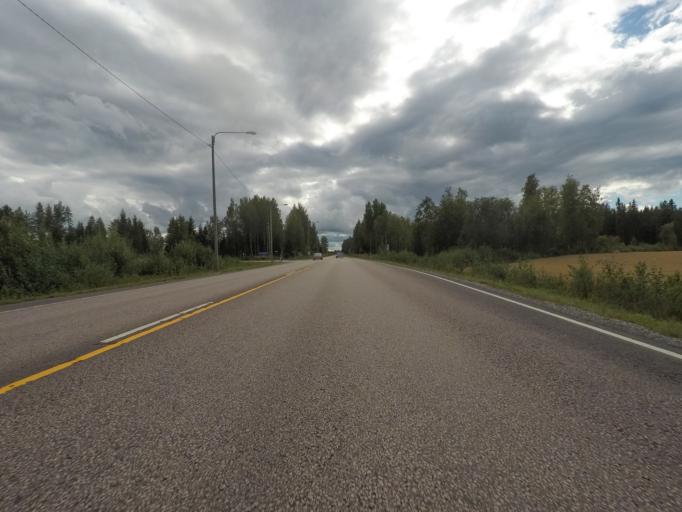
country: FI
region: Paijanne Tavastia
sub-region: Lahti
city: Hartola
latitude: 61.6014
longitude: 26.0087
